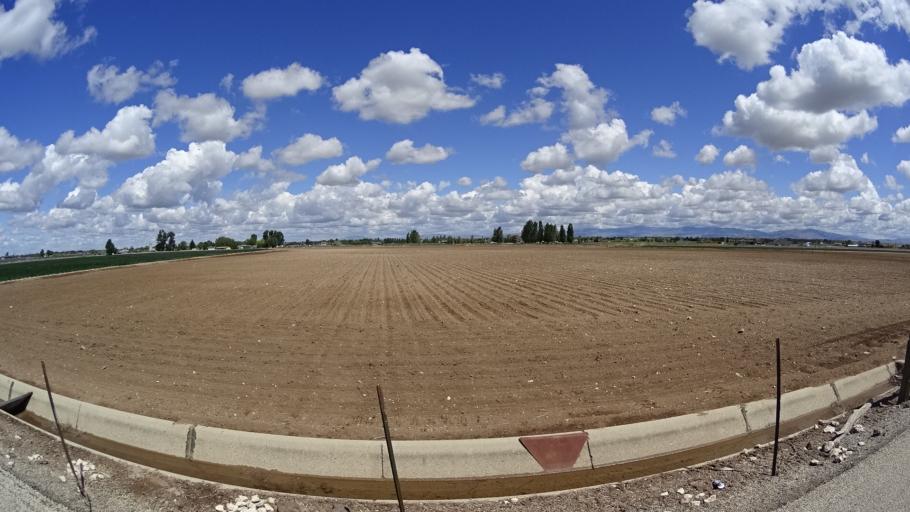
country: US
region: Idaho
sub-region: Ada County
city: Kuna
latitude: 43.4616
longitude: -116.3721
